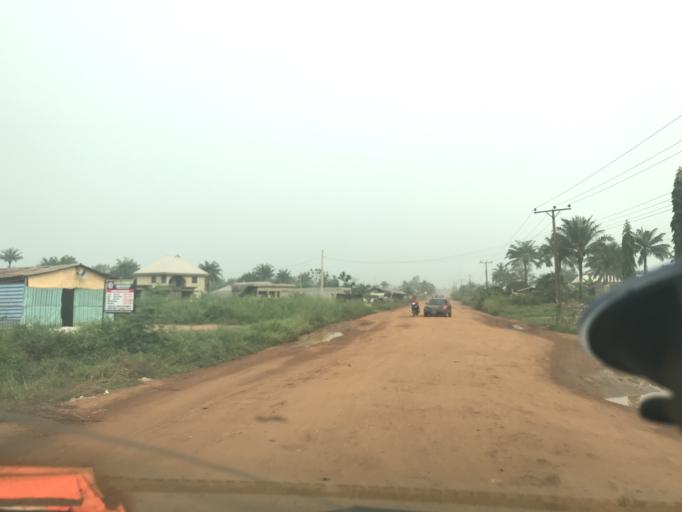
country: NG
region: Ogun
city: Ado Odo
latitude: 6.5345
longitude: 2.9505
